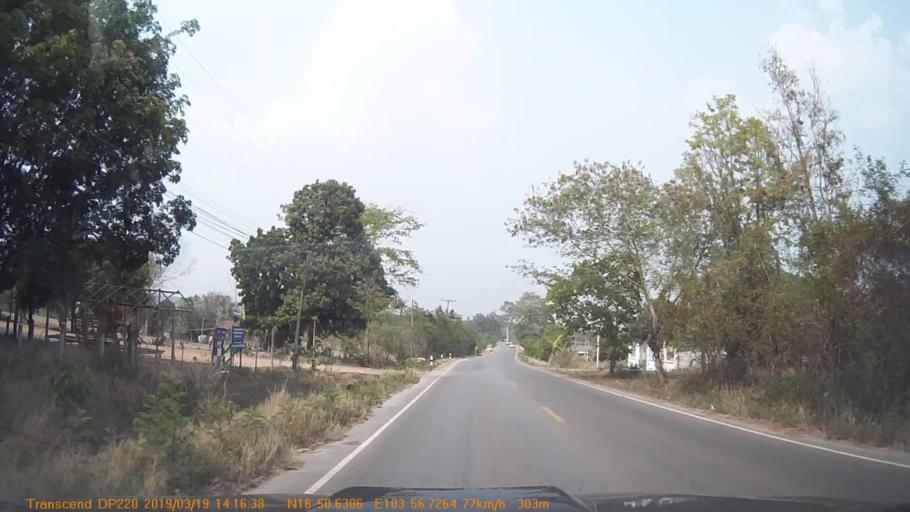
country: TH
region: Kalasin
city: Na Khu
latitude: 16.8444
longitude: 103.9457
